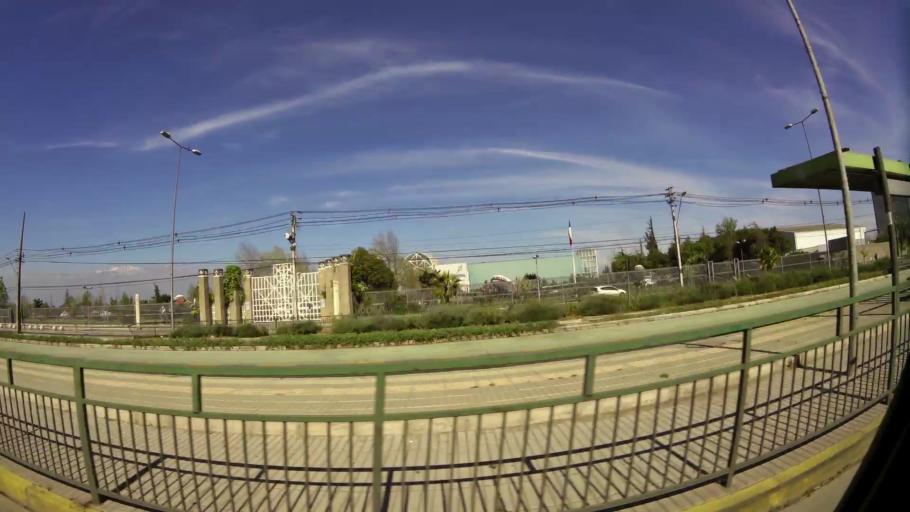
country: CL
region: Santiago Metropolitan
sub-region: Provincia de Santiago
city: Lo Prado
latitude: -33.4863
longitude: -70.6986
